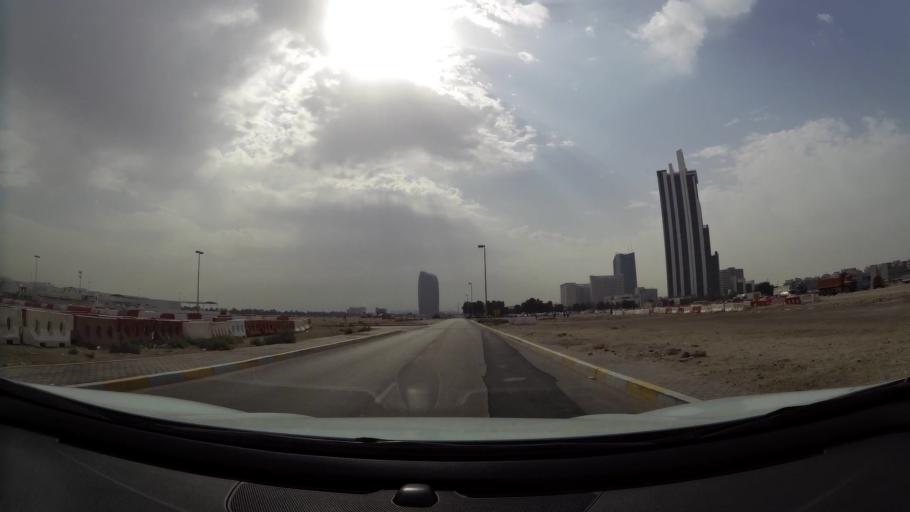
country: AE
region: Abu Dhabi
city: Abu Dhabi
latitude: 24.4649
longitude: 54.3906
